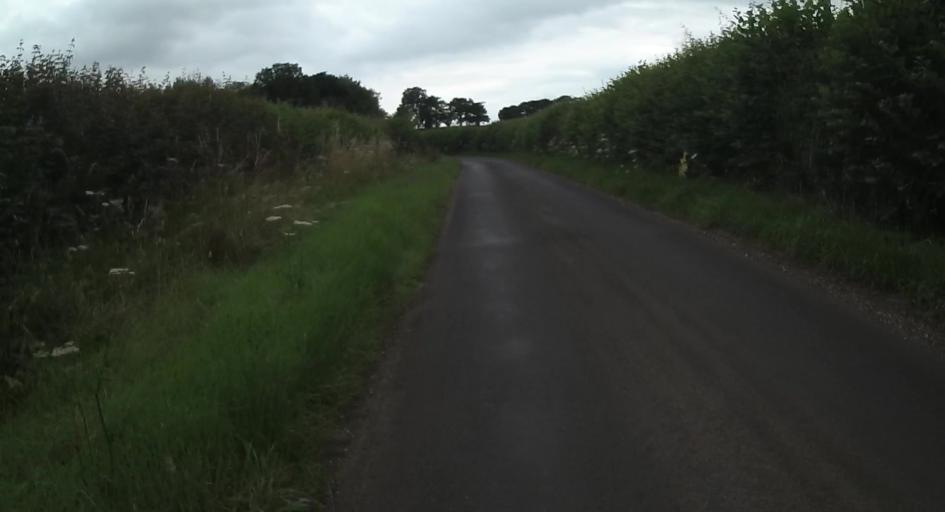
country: GB
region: England
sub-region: Hampshire
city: Swanmore
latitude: 51.0285
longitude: -1.1643
